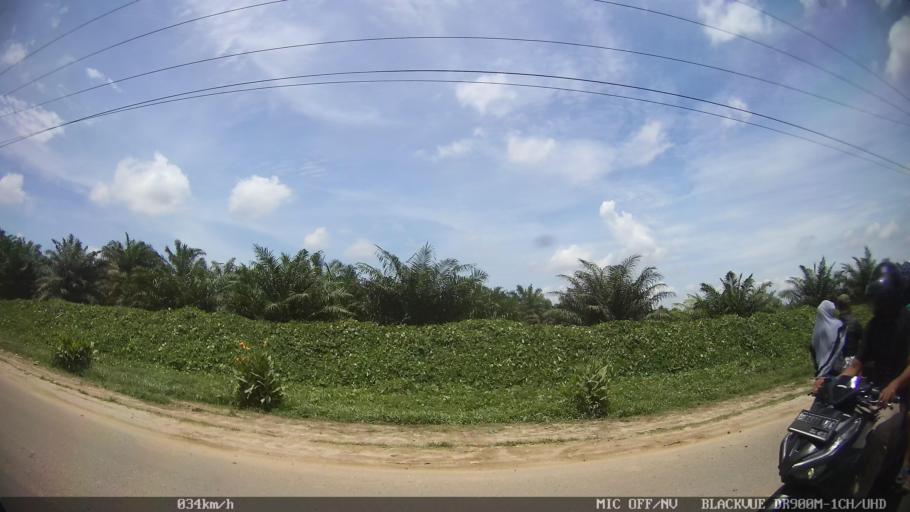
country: ID
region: North Sumatra
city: Perbaungan
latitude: 3.5245
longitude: 98.8885
